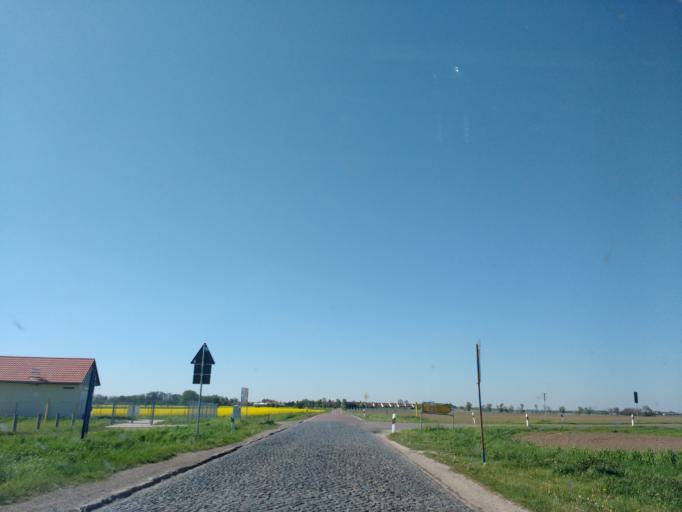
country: DE
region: Saxony-Anhalt
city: Niemberg
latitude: 51.5465
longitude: 12.0680
